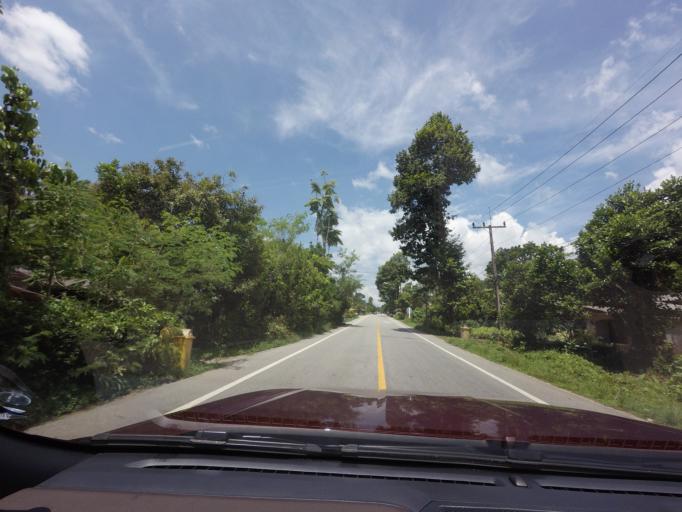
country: TH
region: Narathiwat
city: Ra-ngae
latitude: 6.2356
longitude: 101.6768
